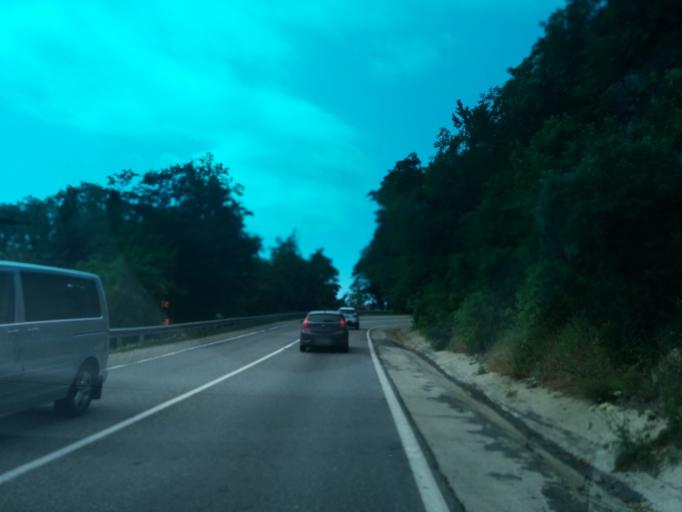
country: RU
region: Krasnodarskiy
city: Nebug
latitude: 44.1747
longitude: 38.9733
